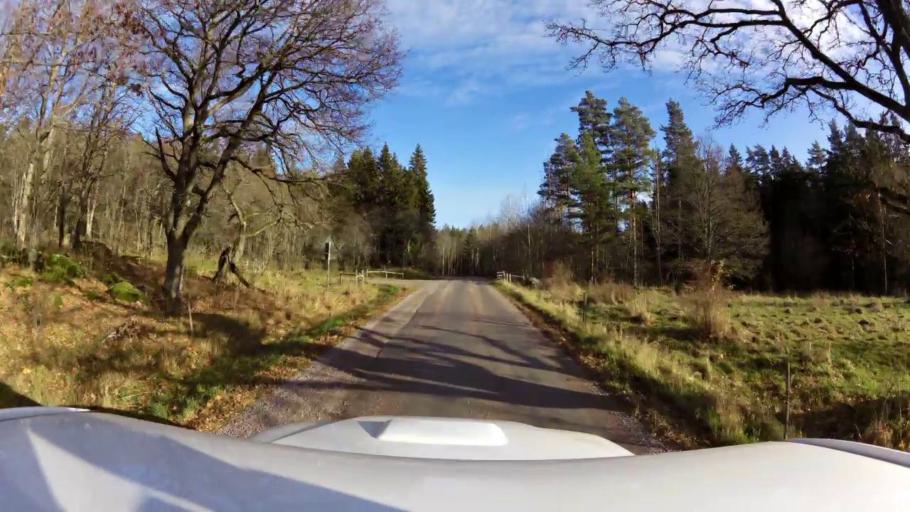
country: SE
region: OEstergoetland
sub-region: Linkopings Kommun
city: Linkoping
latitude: 58.3626
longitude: 15.6028
